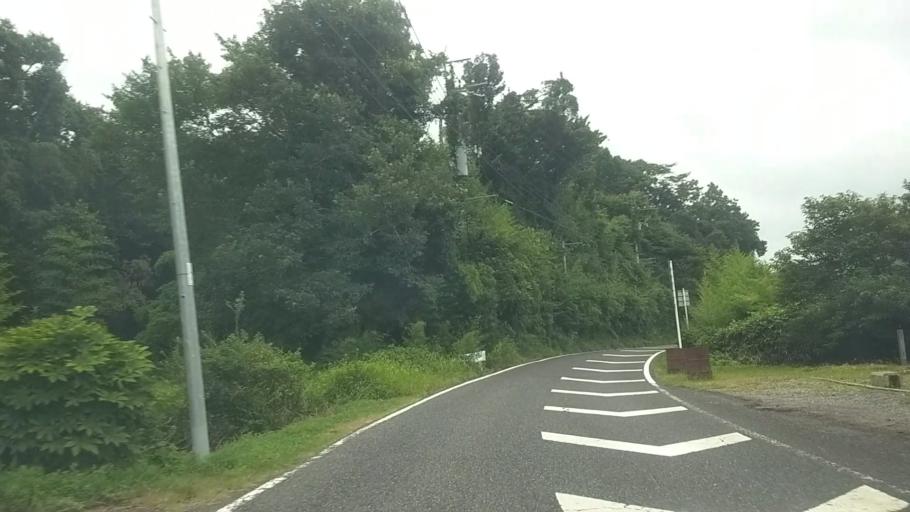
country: JP
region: Chiba
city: Kawaguchi
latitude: 35.2229
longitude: 140.0208
